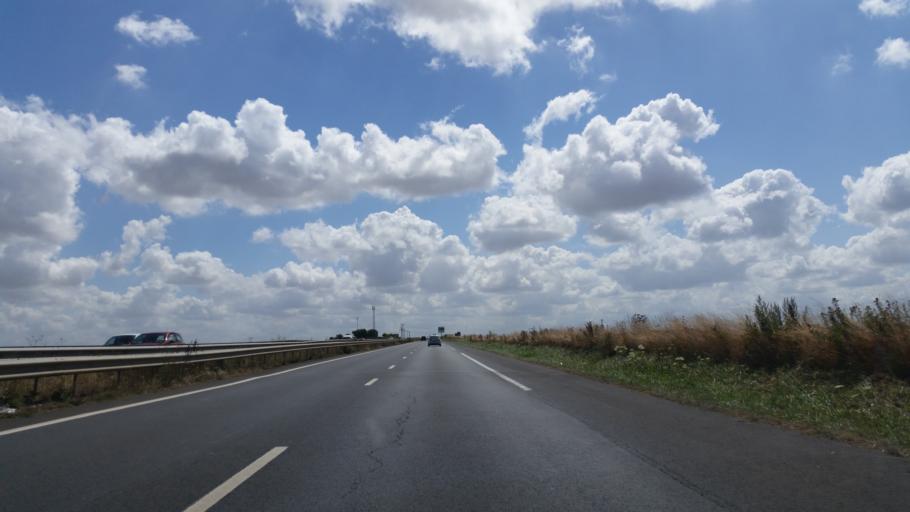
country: FR
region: Lower Normandy
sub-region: Departement du Calvados
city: Bourguebus
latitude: 49.1194
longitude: -0.3240
